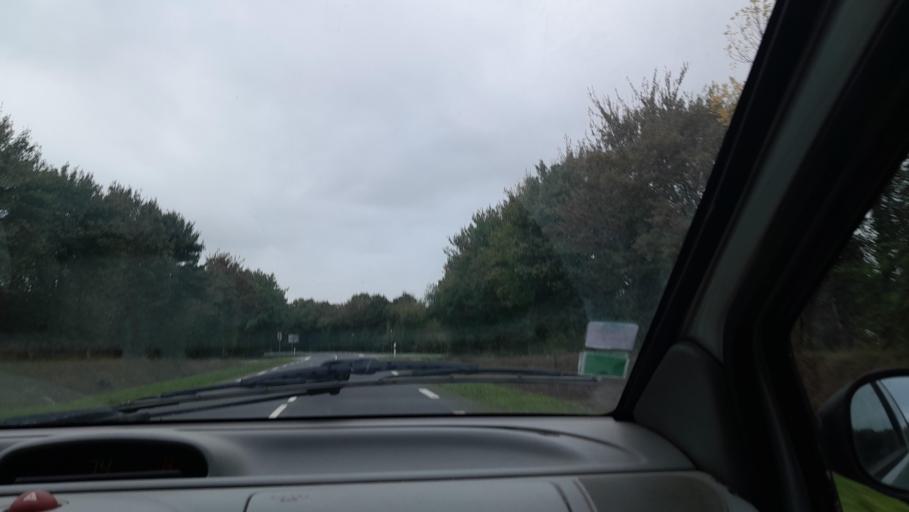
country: FR
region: Pays de la Loire
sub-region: Departement de la Loire-Atlantique
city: Saint-Mars-la-Jaille
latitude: 47.5294
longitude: -1.1807
